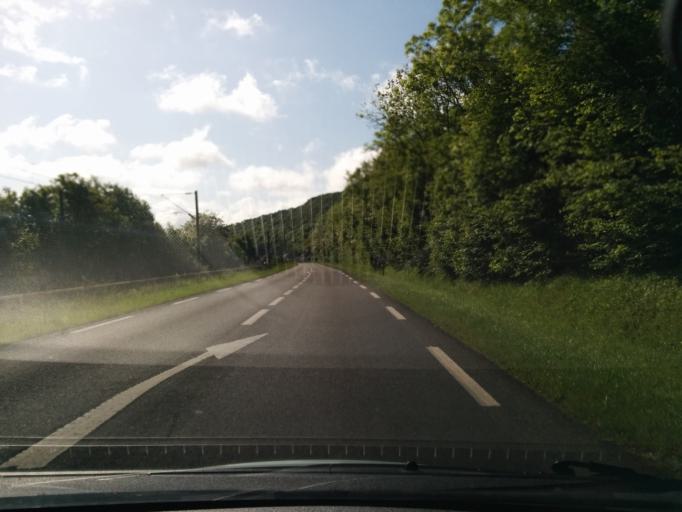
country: FR
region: Ile-de-France
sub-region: Departement des Yvelines
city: Bennecourt
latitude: 49.0385
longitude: 1.5392
